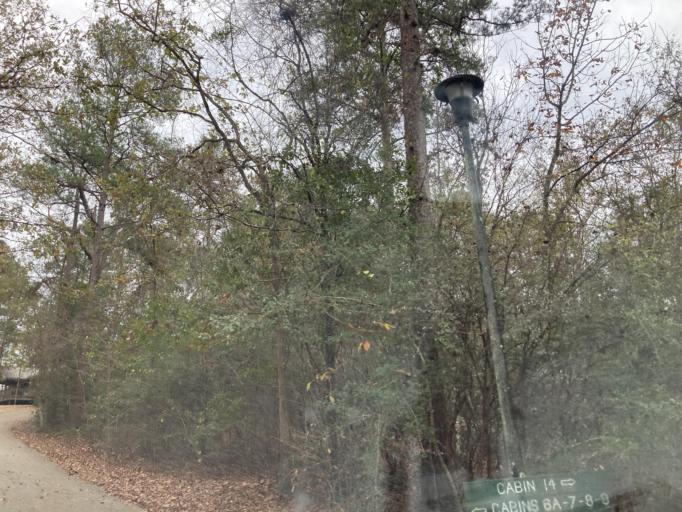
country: US
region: Mississippi
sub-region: Lamar County
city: Lumberton
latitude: 31.0821
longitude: -89.4985
